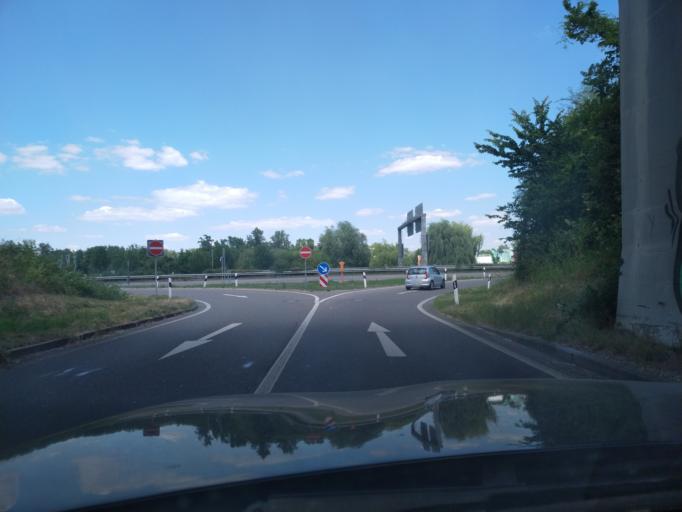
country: DE
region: Rheinland-Pfalz
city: Worth am Rhein
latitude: 49.0391
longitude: 8.2910
